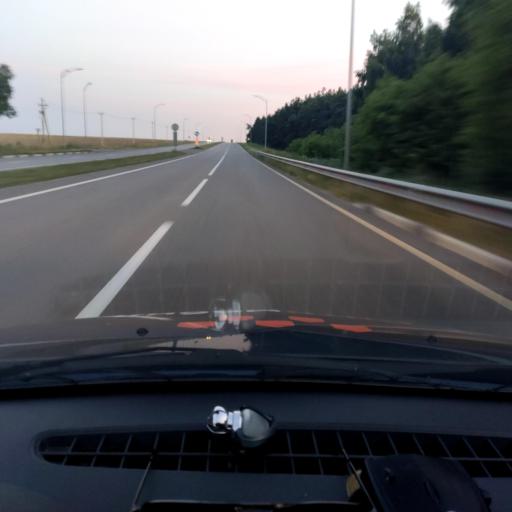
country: RU
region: Belgorod
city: Staryy Oskol
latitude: 51.4024
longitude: 37.8769
